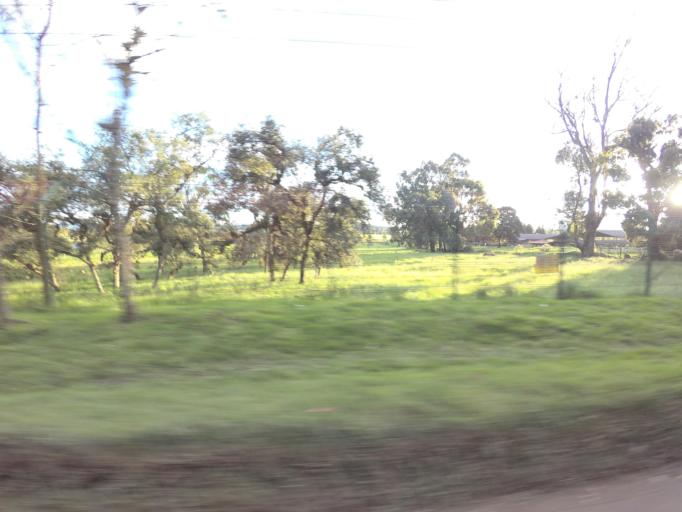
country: CO
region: Cundinamarca
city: Cota
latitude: 4.7935
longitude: -74.0301
